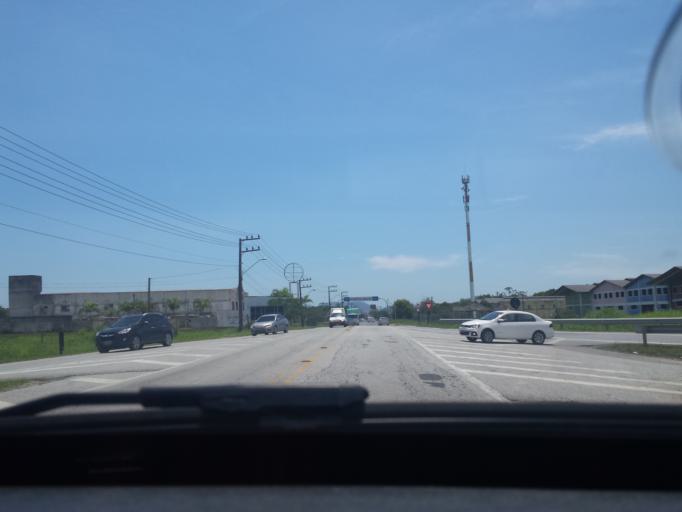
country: BR
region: Santa Catarina
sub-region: Porto Belo
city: Porto Belo
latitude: -27.1624
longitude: -48.6096
